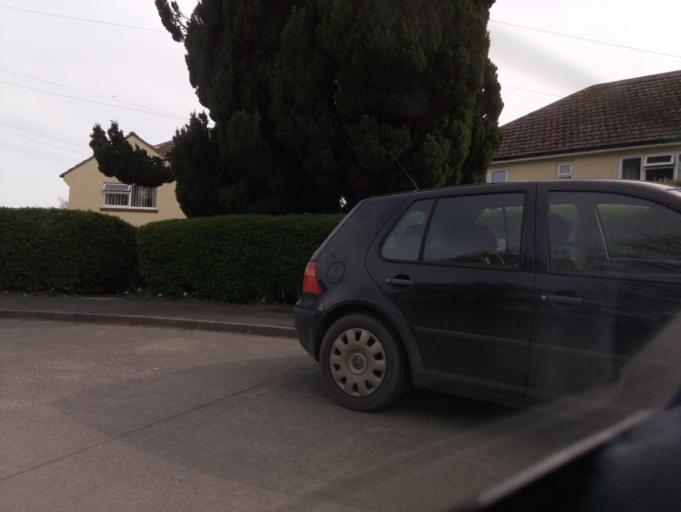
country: GB
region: England
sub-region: Dorset
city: Sherborne
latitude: 50.9564
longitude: -2.5163
